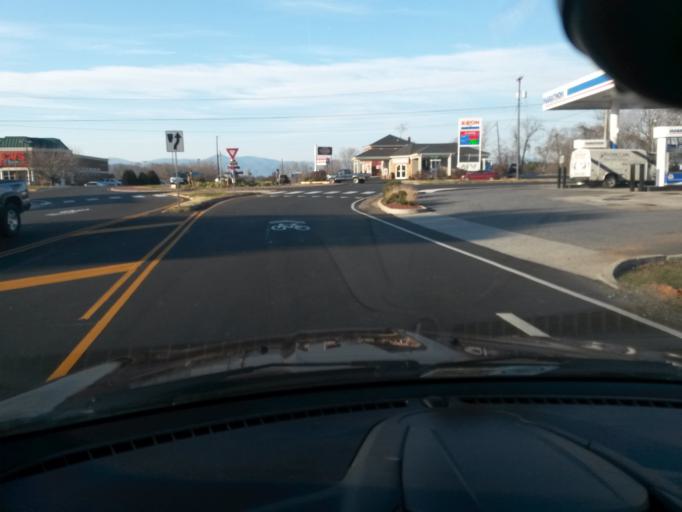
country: US
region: Virginia
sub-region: Amherst County
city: Amherst
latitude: 37.5877
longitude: -79.0495
